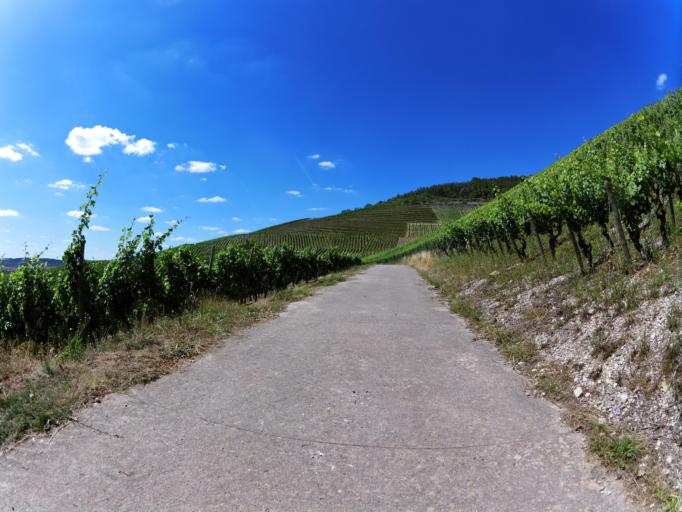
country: DE
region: Bavaria
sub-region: Regierungsbezirk Unterfranken
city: Thungersheim
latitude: 49.8879
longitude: 9.8525
